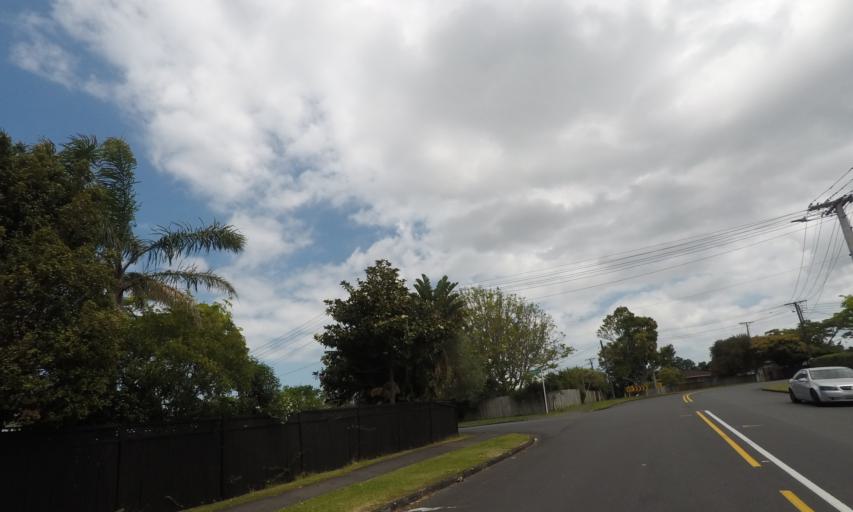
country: NZ
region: Auckland
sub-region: Auckland
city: Waitakere
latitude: -36.9056
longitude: 174.6691
